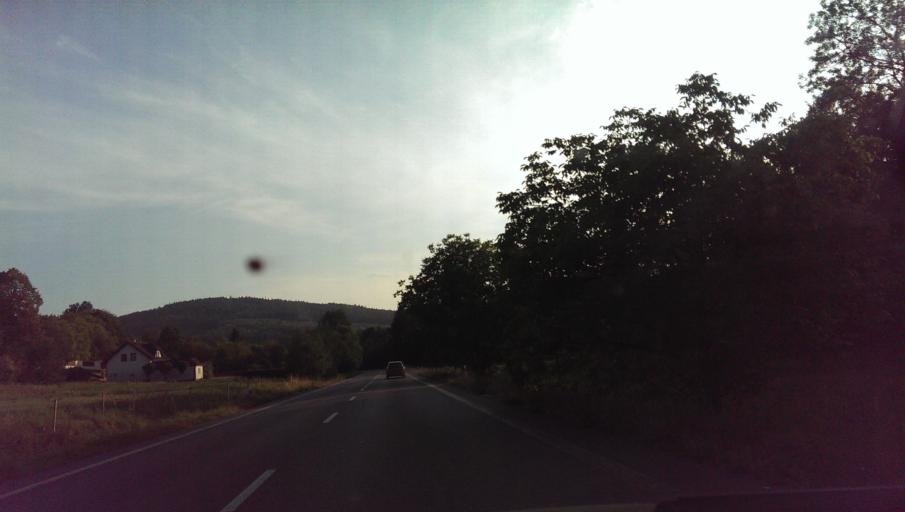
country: CZ
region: Zlin
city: Pozlovice
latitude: 49.1303
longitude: 17.8038
